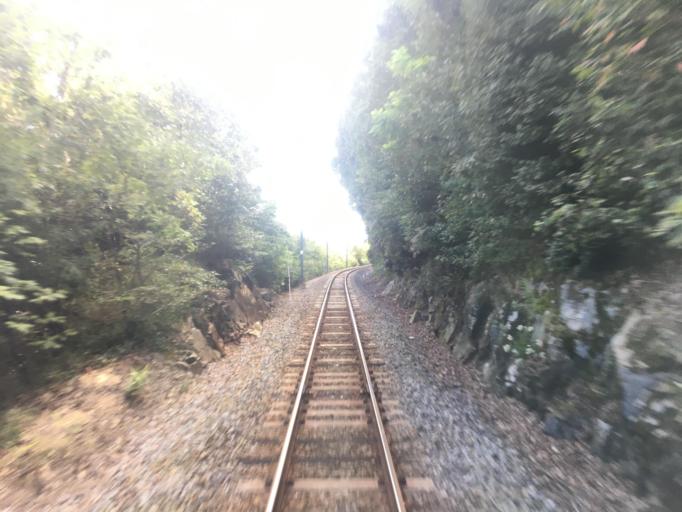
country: JP
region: Hyogo
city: Ono
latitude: 34.8286
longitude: 134.9265
